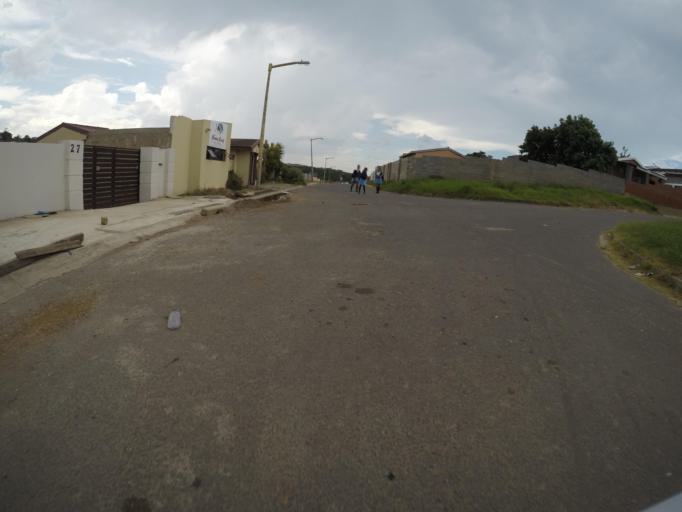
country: ZA
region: Eastern Cape
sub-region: Buffalo City Metropolitan Municipality
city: East London
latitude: -33.0201
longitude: 27.8668
